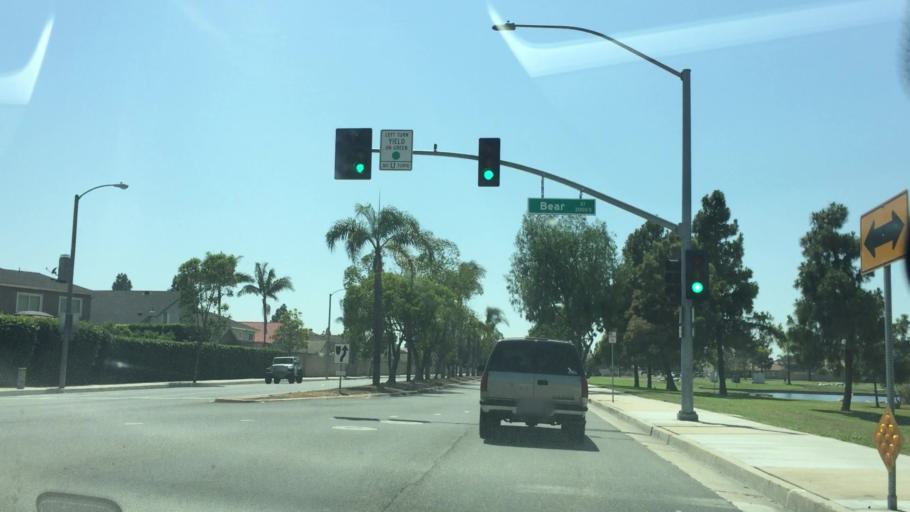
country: US
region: California
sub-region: Orange County
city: Santa Ana
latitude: 33.7074
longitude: -117.8922
